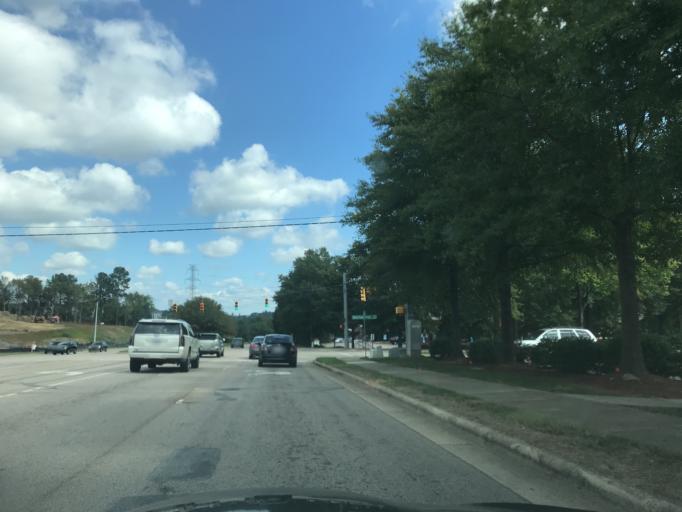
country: US
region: North Carolina
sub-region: Wake County
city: Wake Forest
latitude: 35.9424
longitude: -78.5599
